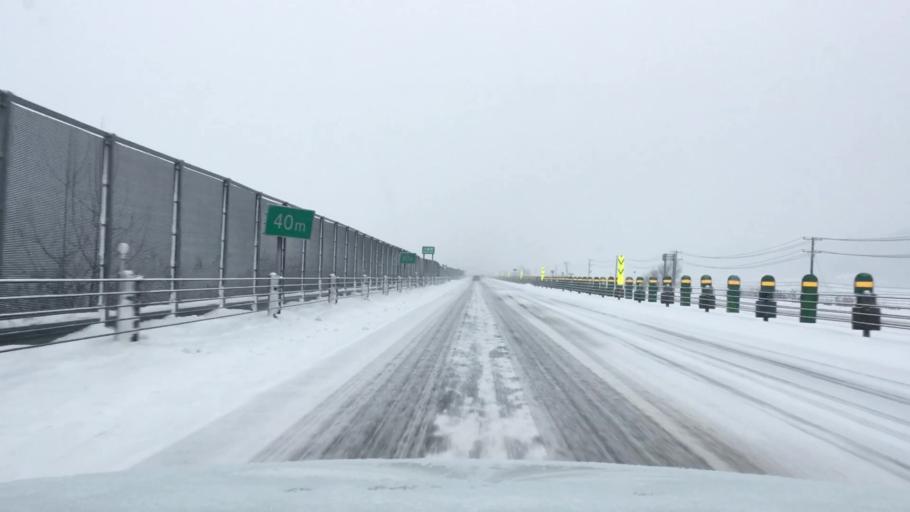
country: JP
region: Akita
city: Hanawa
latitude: 40.2832
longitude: 140.7602
